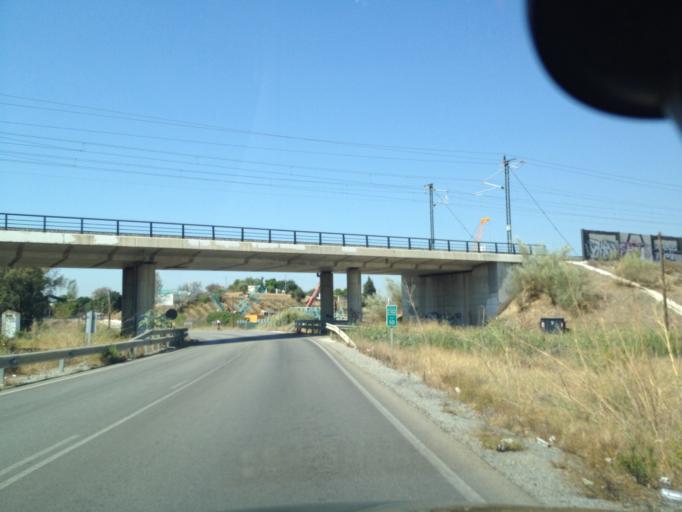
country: ES
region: Andalusia
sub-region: Provincia de Malaga
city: Estacion de Cartama
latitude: 36.7324
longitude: -4.5906
